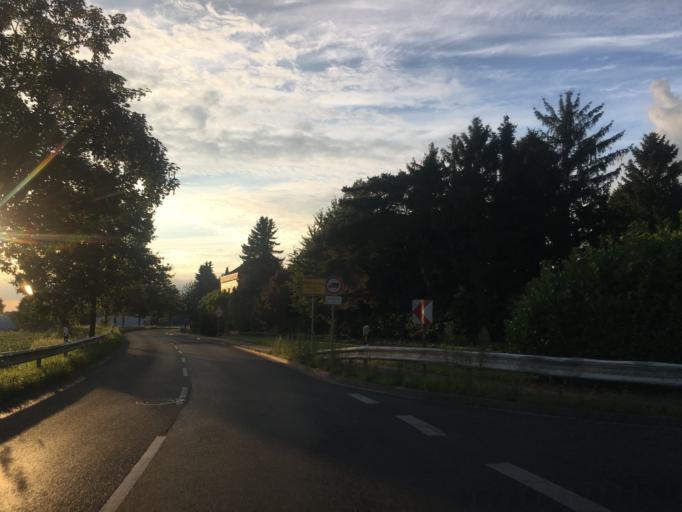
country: DE
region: North Rhine-Westphalia
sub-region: Regierungsbezirk Koln
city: Linnich
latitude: 50.9960
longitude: 6.2879
